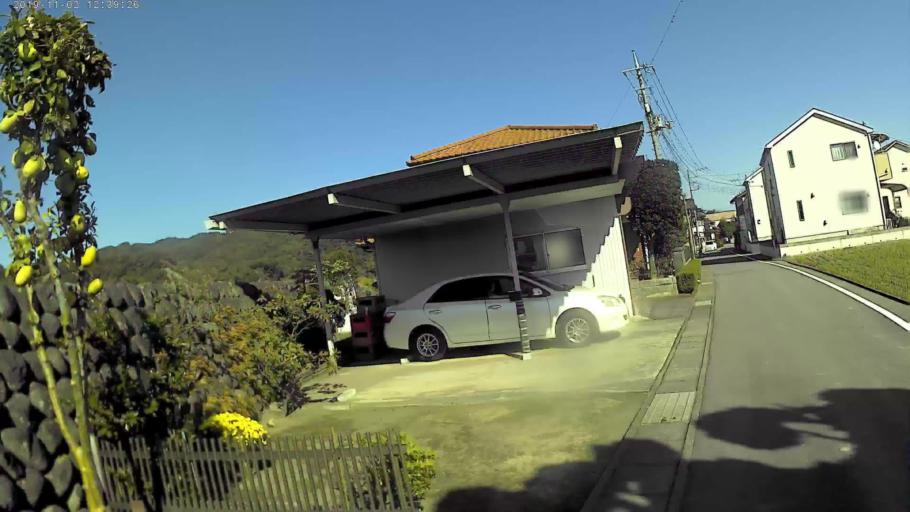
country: JP
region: Gunma
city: Annaka
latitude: 36.3339
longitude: 138.9130
